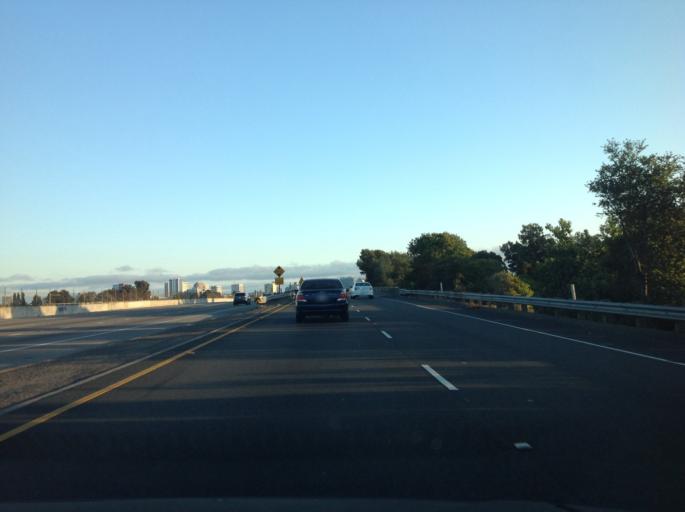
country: US
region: California
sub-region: Alameda County
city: Emeryville
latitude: 37.8362
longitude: -122.2661
